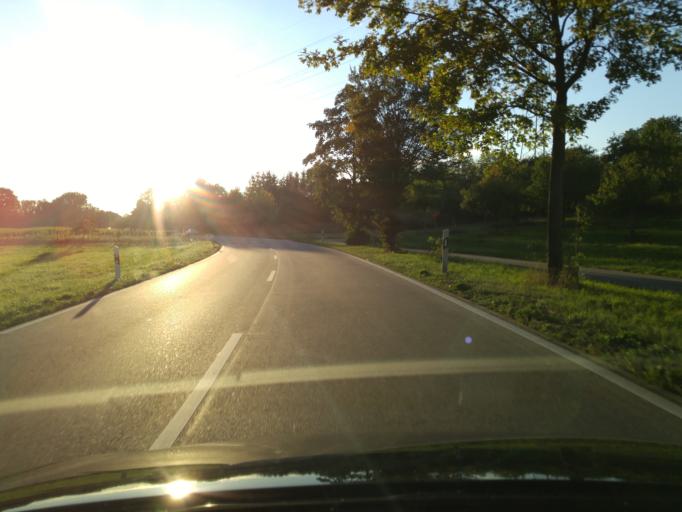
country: DE
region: Baden-Wuerttemberg
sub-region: Regierungsbezirk Stuttgart
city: Bad Wimpfen
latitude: 49.1904
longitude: 9.1658
